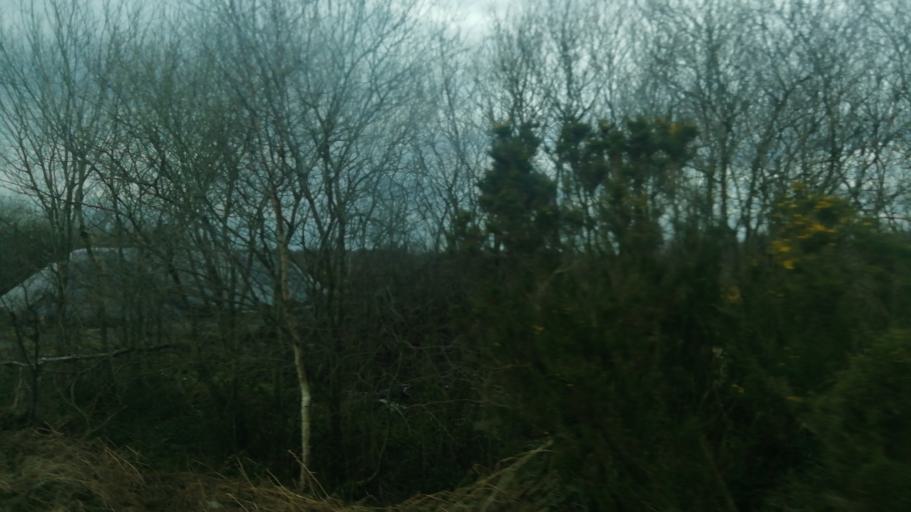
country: IE
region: Leinster
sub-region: Kildare
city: Derrinturn
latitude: 53.2823
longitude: -6.9054
